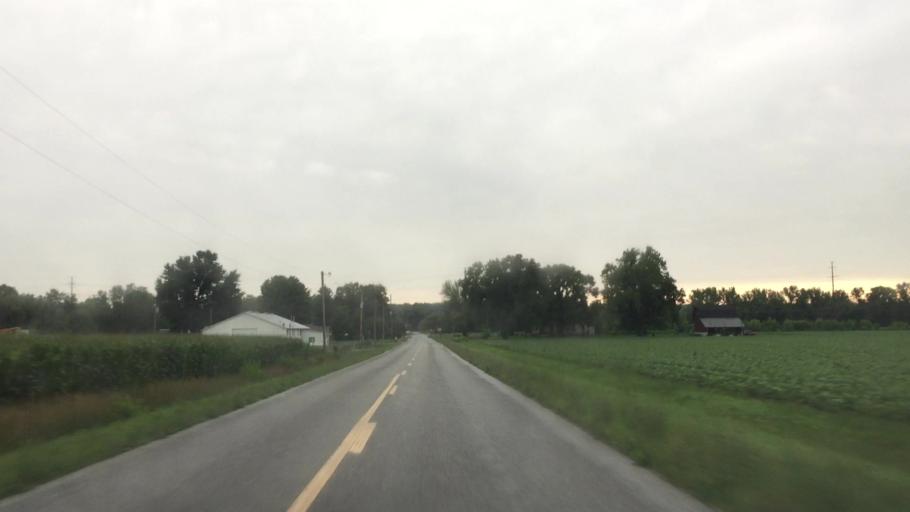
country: US
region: Iowa
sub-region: Lee County
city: Fort Madison
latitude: 40.6146
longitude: -91.2819
